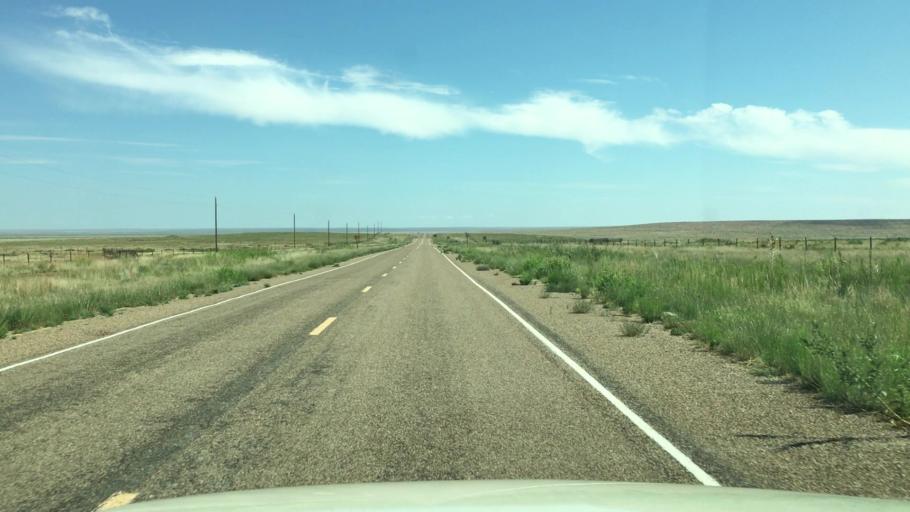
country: US
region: New Mexico
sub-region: De Baca County
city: Fort Sumner
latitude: 33.9949
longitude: -104.5686
